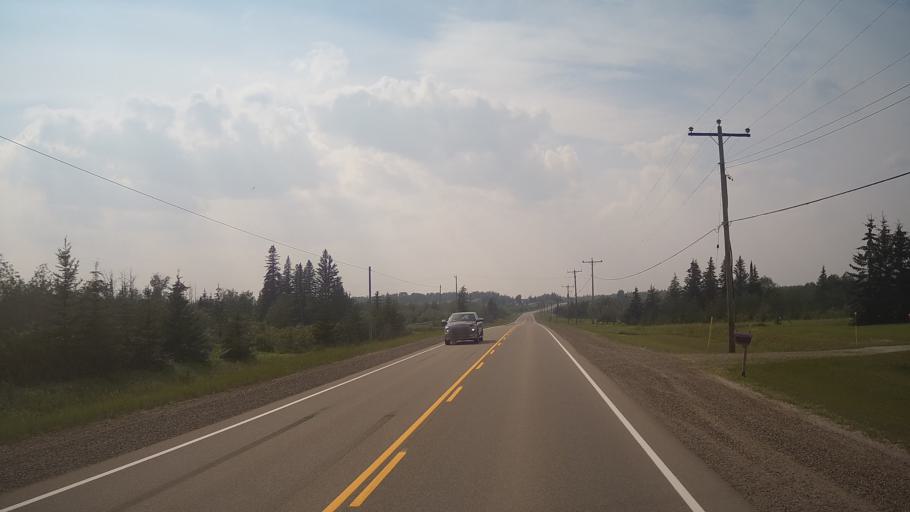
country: CA
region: Ontario
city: Kapuskasing
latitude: 49.4316
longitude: -82.5039
